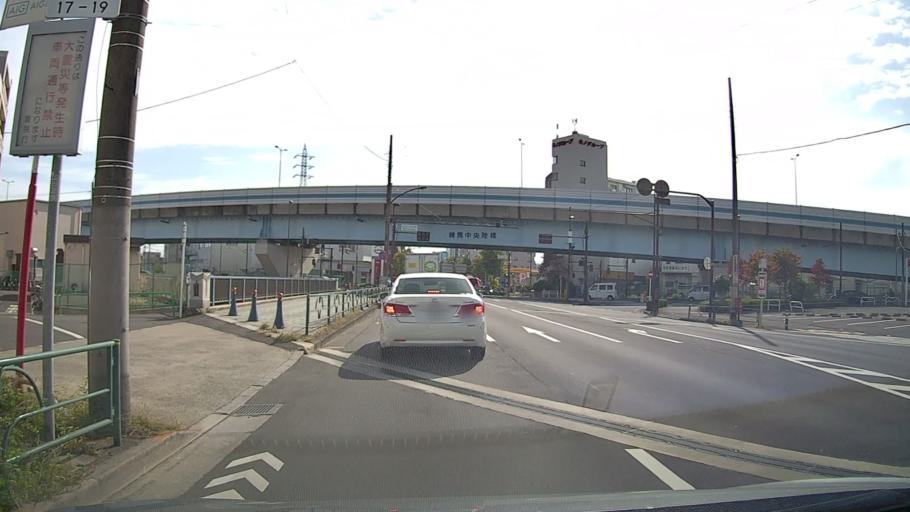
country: JP
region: Saitama
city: Wako
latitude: 35.7452
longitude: 139.6281
